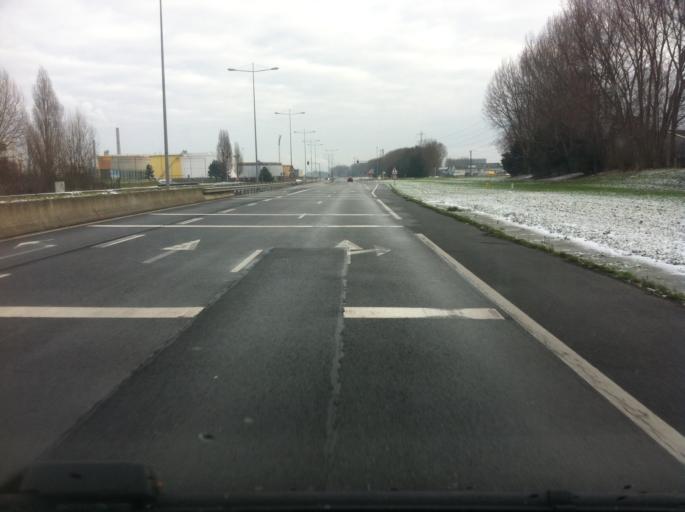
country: FR
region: Haute-Normandie
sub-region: Departement de la Seine-Maritime
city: Harfleur
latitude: 49.4859
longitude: 0.2212
